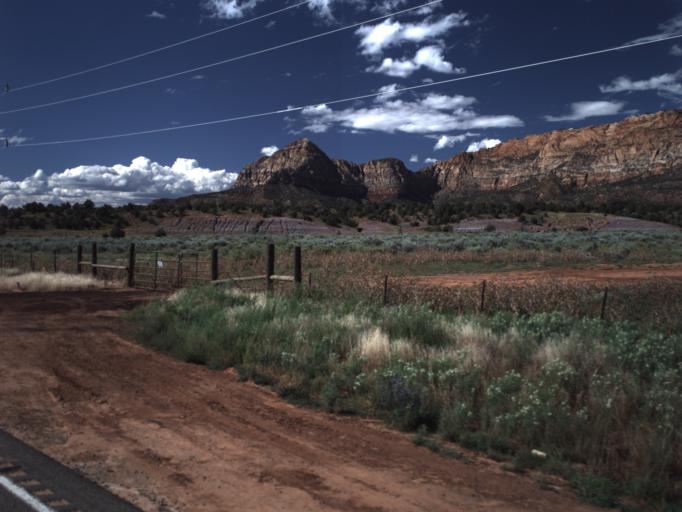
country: US
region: Arizona
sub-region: Mohave County
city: Colorado City
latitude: 37.0171
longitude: -113.0288
